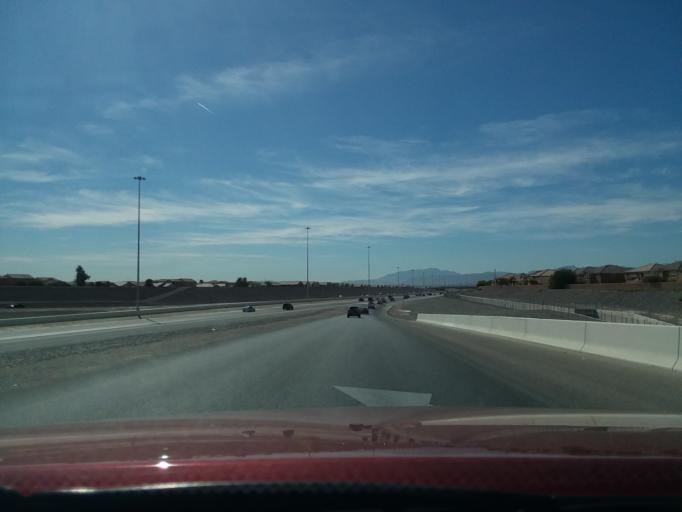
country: US
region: Nevada
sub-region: Clark County
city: North Las Vegas
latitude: 36.2896
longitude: -115.1819
